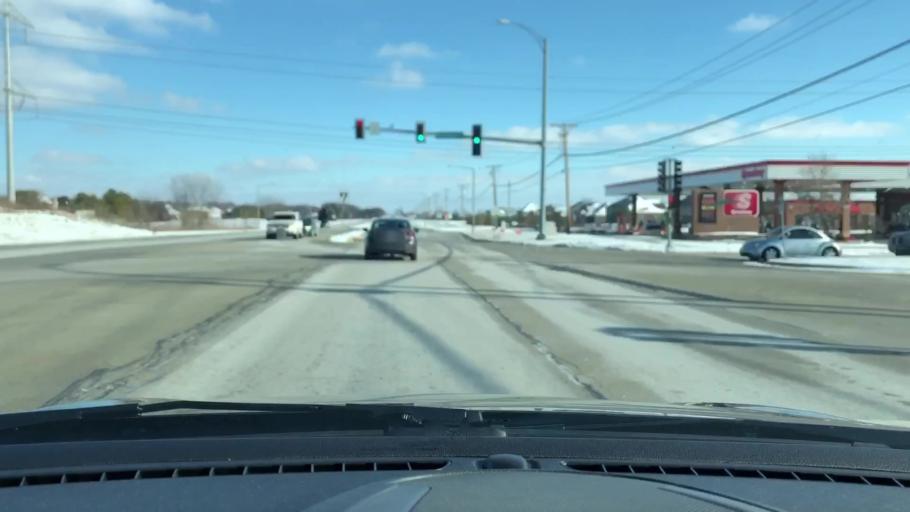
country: US
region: Illinois
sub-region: Will County
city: New Lenox
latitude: 41.4832
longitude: -87.9574
